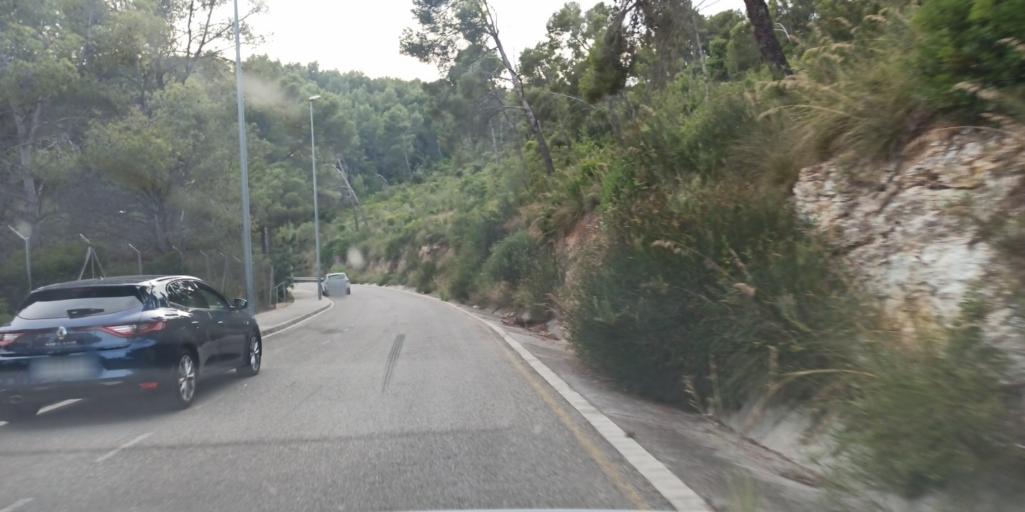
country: ES
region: Catalonia
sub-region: Provincia de Barcelona
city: Gava
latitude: 41.3092
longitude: 1.9878
